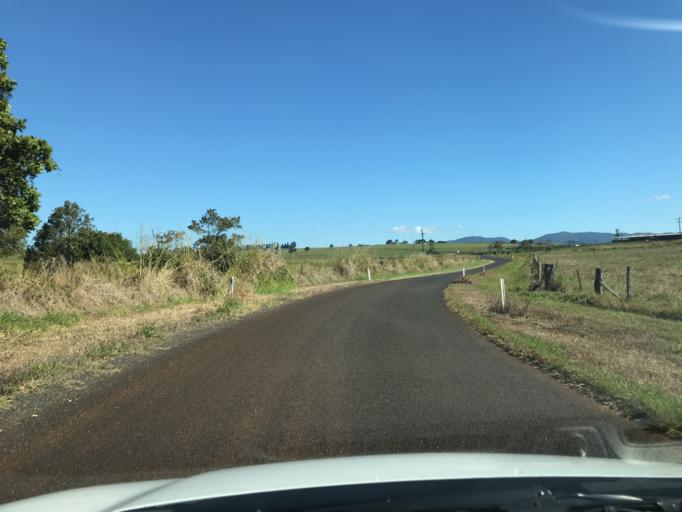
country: AU
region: Queensland
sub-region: Tablelands
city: Atherton
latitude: -17.2961
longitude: 145.5441
